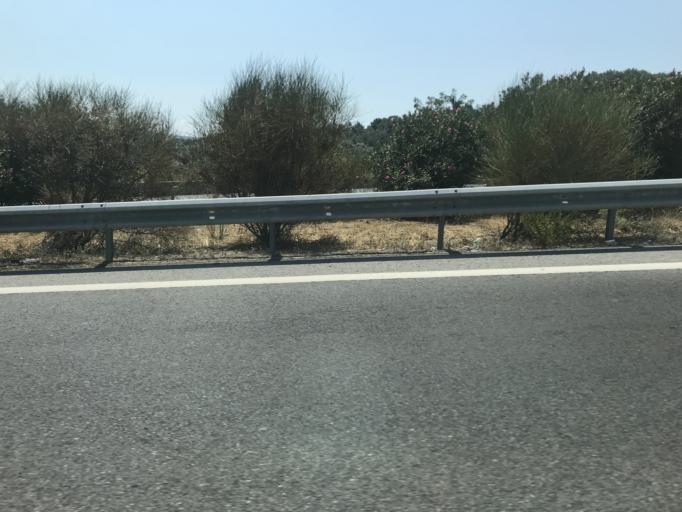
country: TR
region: Izmir
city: Urla
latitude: 38.3499
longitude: 26.8487
